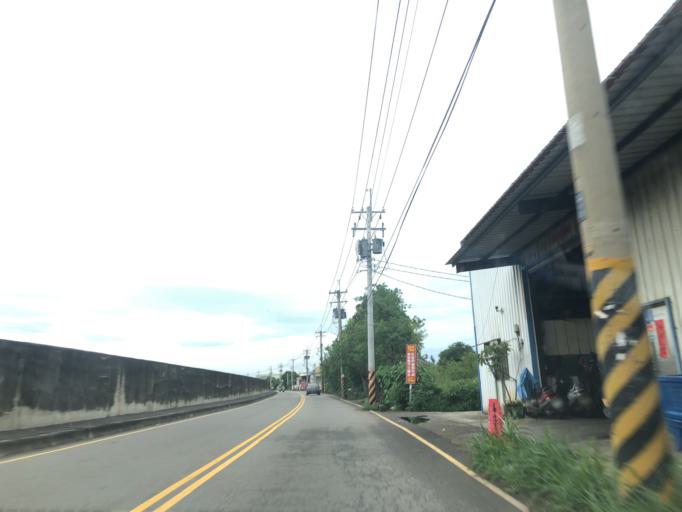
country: TW
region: Taiwan
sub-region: Taichung City
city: Taichung
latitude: 24.1136
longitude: 120.7019
